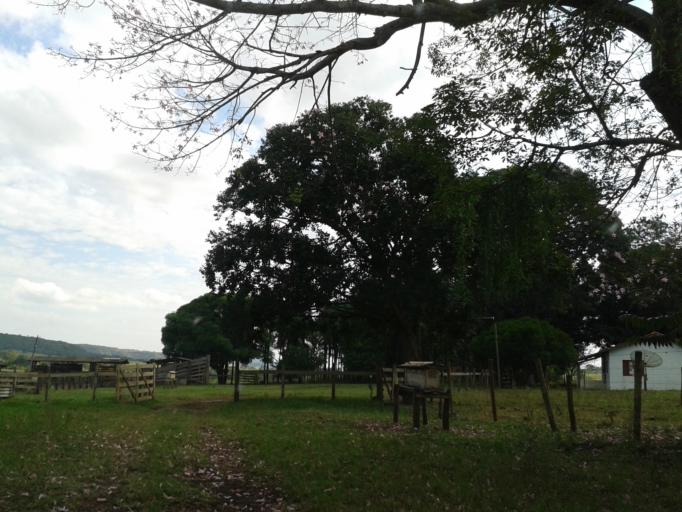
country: BR
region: Minas Gerais
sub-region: Campina Verde
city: Campina Verde
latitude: -19.3940
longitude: -49.6776
